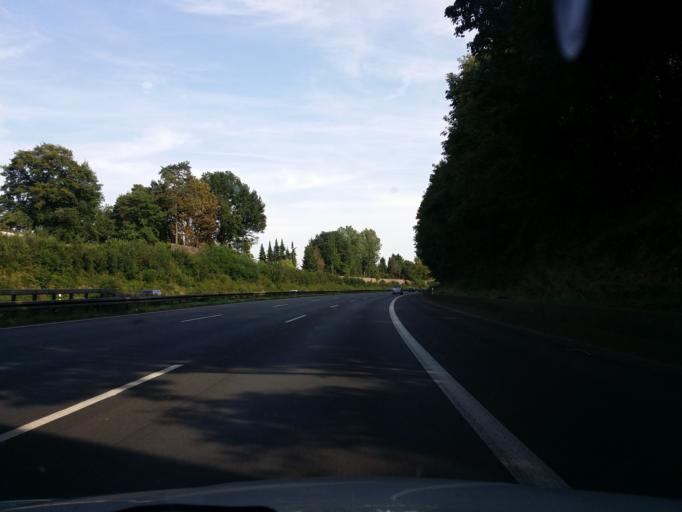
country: DE
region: North Rhine-Westphalia
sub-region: Regierungsbezirk Koln
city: Rosrath
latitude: 50.8951
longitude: 7.1643
